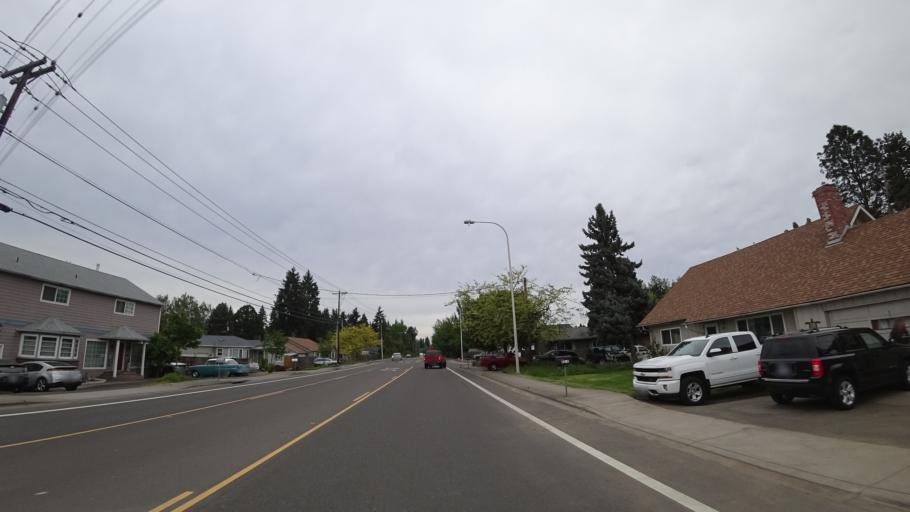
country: US
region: Oregon
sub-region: Washington County
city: Hillsboro
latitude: 45.5022
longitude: -122.9310
